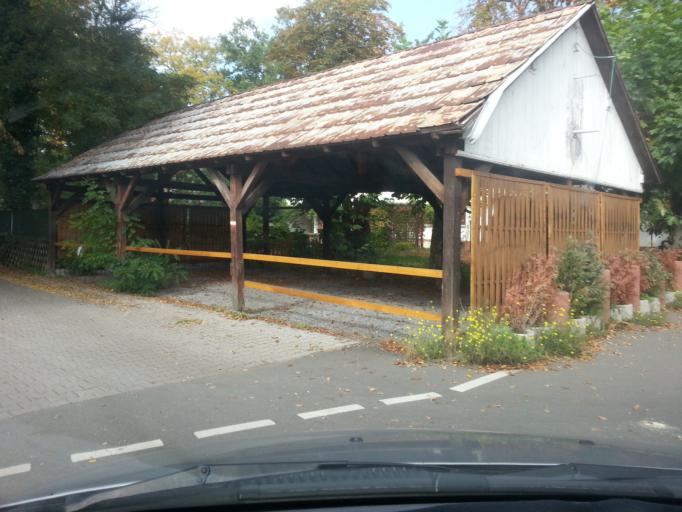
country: DE
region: Rheinland-Pfalz
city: Hassloch
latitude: 49.3484
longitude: 8.2746
